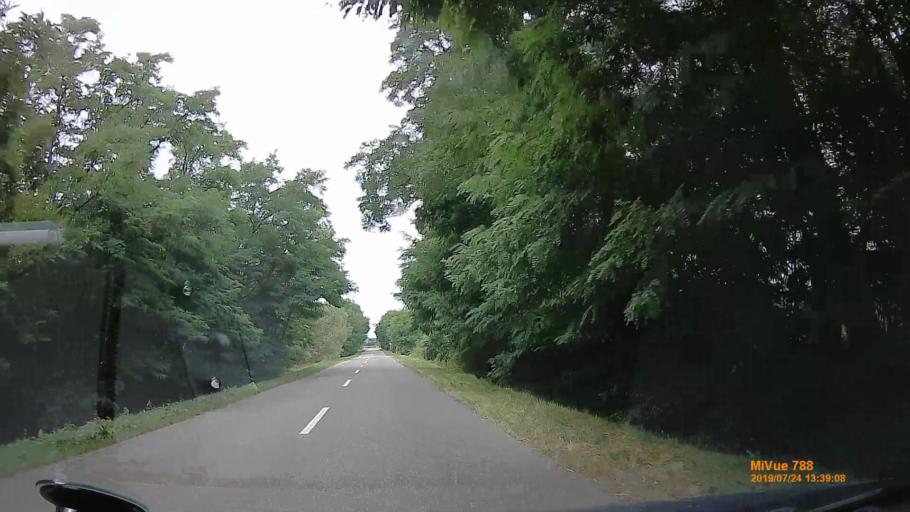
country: HU
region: Szabolcs-Szatmar-Bereg
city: Aranyosapati
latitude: 48.2360
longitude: 22.3197
